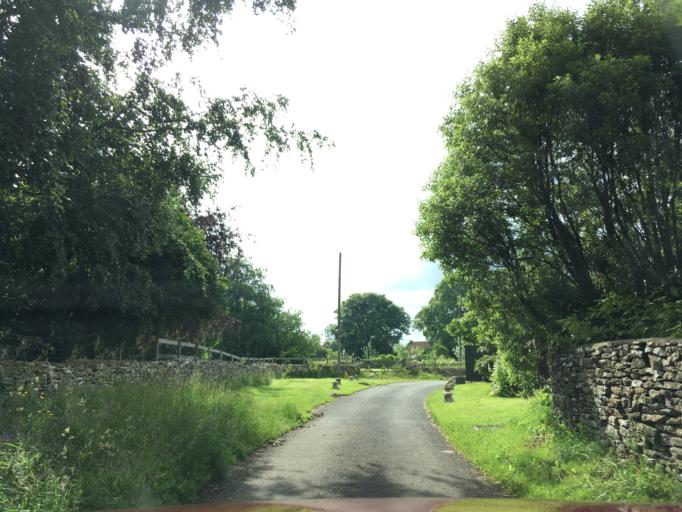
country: GB
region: England
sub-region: South Gloucestershire
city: Hinton
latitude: 51.5061
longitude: -2.3397
